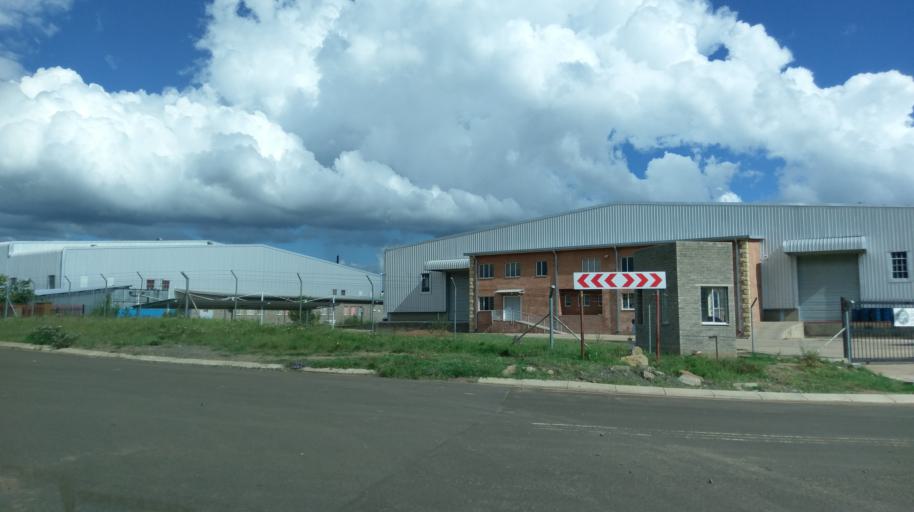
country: LS
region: Maseru
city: Maseru
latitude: -29.3801
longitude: 27.4845
